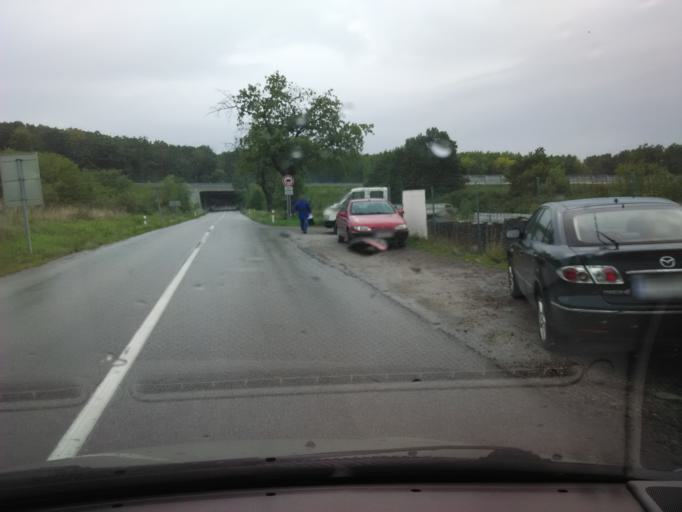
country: SK
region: Nitriansky
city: Tlmace
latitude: 48.3540
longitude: 18.4795
